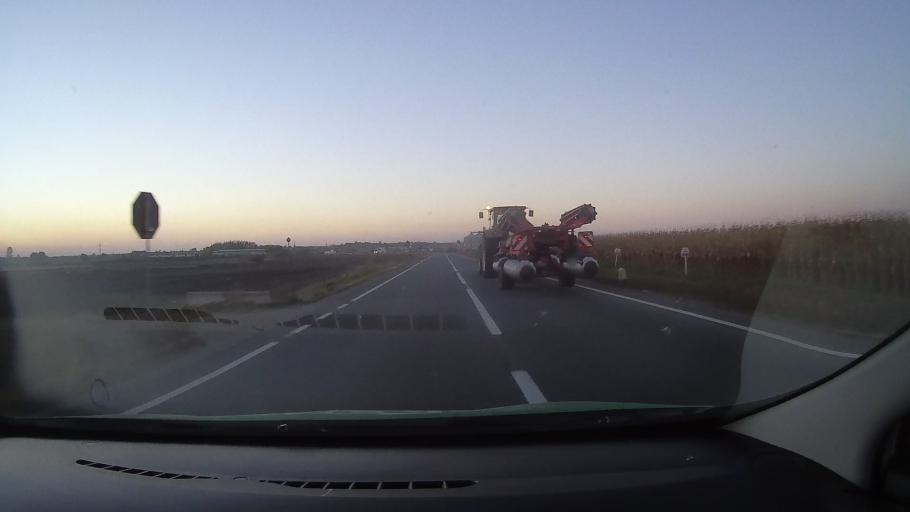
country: RO
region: Bihor
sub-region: Comuna Tarcea
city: Tarcea
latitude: 47.4499
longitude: 22.1850
